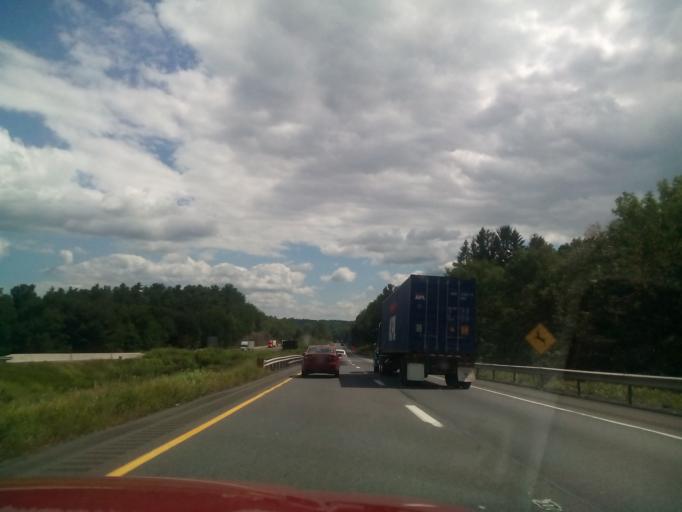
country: US
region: Pennsylvania
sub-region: Monroe County
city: Tannersville
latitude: 41.0237
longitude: -75.3058
